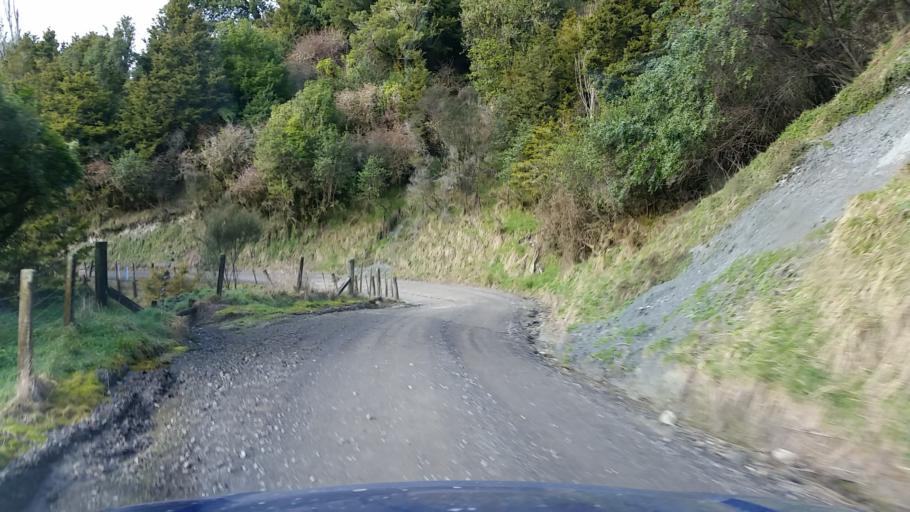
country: NZ
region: Taranaki
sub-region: New Plymouth District
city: Waitara
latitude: -39.0732
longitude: 174.7996
